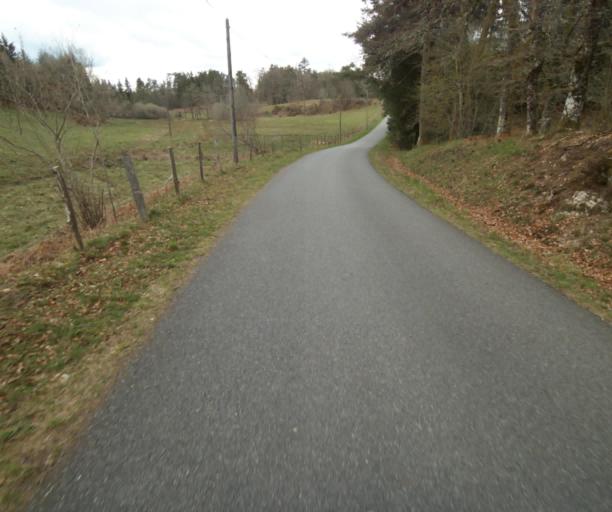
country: FR
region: Limousin
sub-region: Departement de la Correze
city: Correze
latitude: 45.3063
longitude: 1.9313
